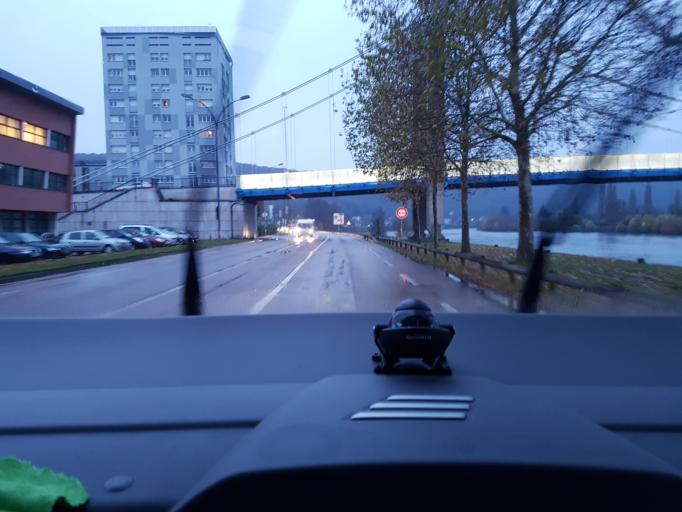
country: FR
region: Haute-Normandie
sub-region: Departement de la Seine-Maritime
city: Elbeuf
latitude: 49.2931
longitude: 1.0051
